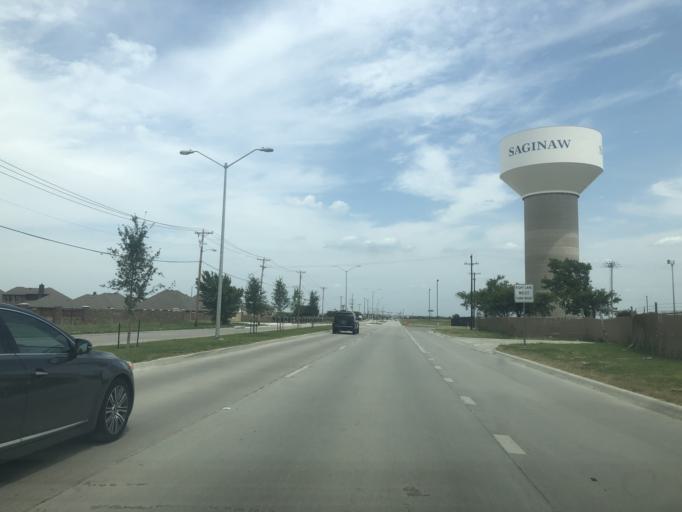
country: US
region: Texas
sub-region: Tarrant County
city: Saginaw
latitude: 32.8837
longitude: -97.3713
